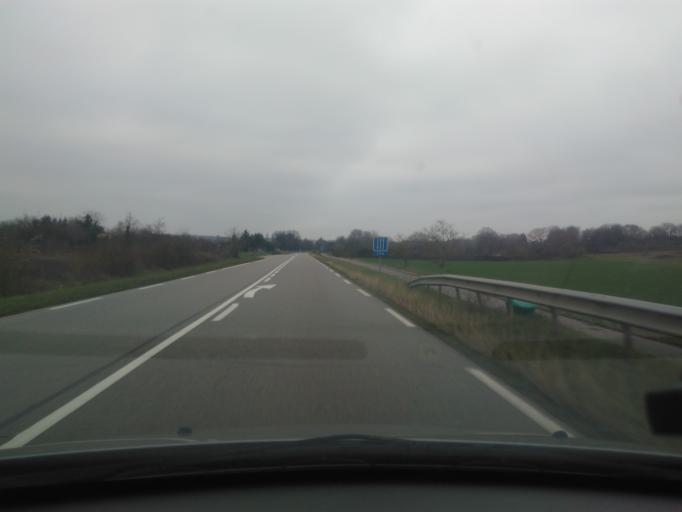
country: FR
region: Centre
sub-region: Departement de l'Indre
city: Saint-Gaultier
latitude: 46.6426
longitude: 1.4192
